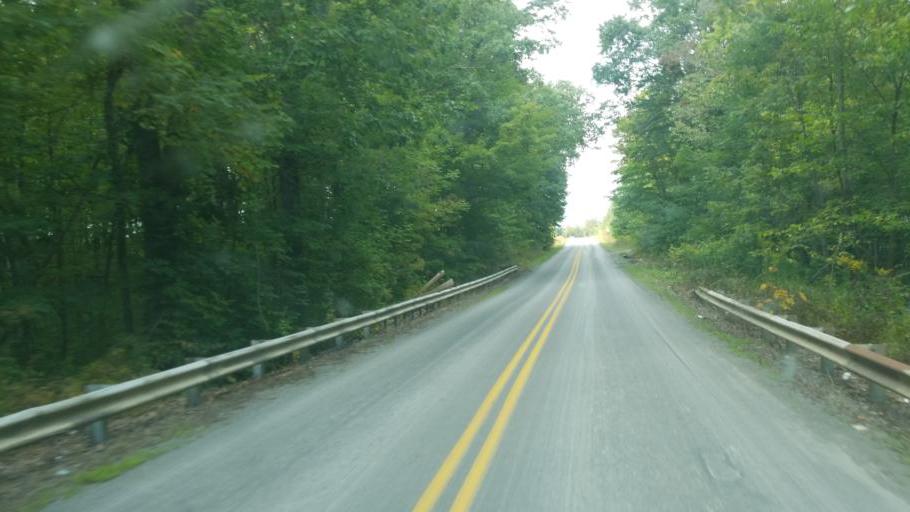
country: US
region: Pennsylvania
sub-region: Crawford County
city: Conneaut Lakeshore
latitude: 41.5210
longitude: -80.3372
